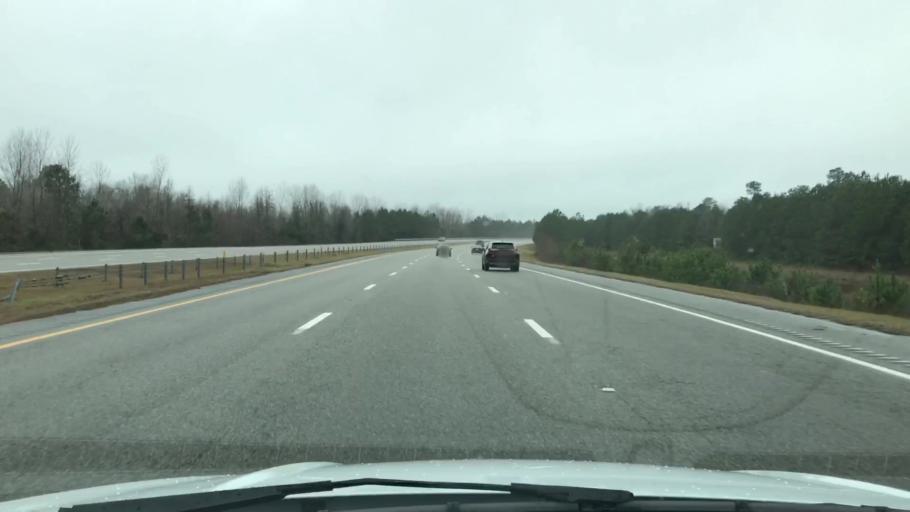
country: US
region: South Carolina
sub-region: Horry County
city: Myrtle Beach
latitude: 33.7492
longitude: -78.8780
